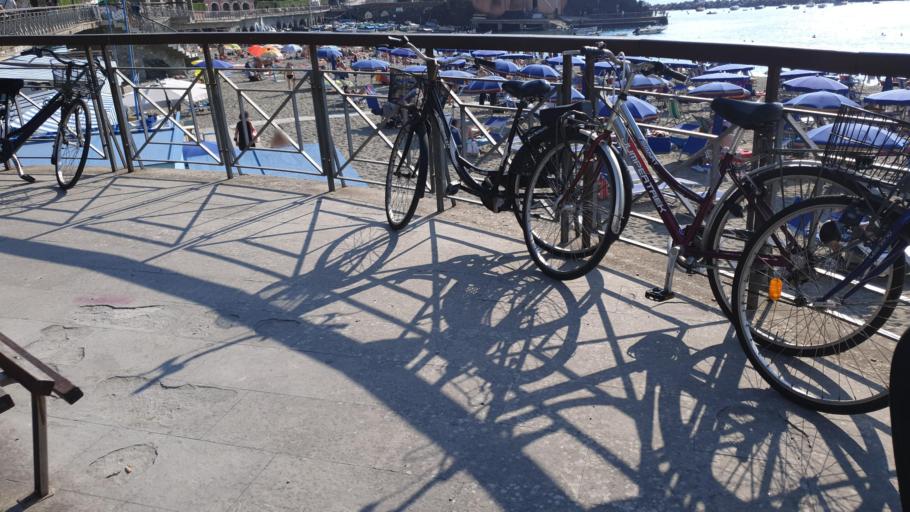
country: IT
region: Liguria
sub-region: Provincia di La Spezia
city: Levanto
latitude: 44.1672
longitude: 9.6105
